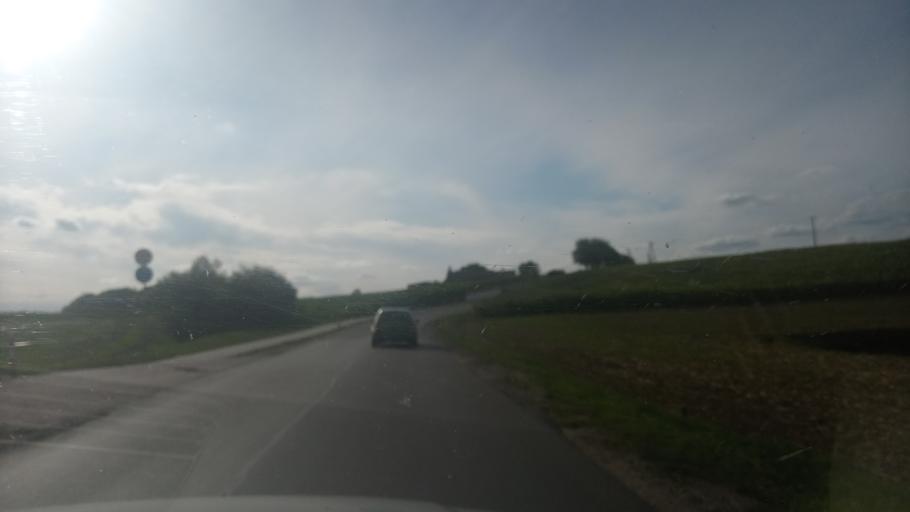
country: PL
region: Greater Poland Voivodeship
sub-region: Powiat pilski
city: Lobzenica
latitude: 53.2518
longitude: 17.2729
